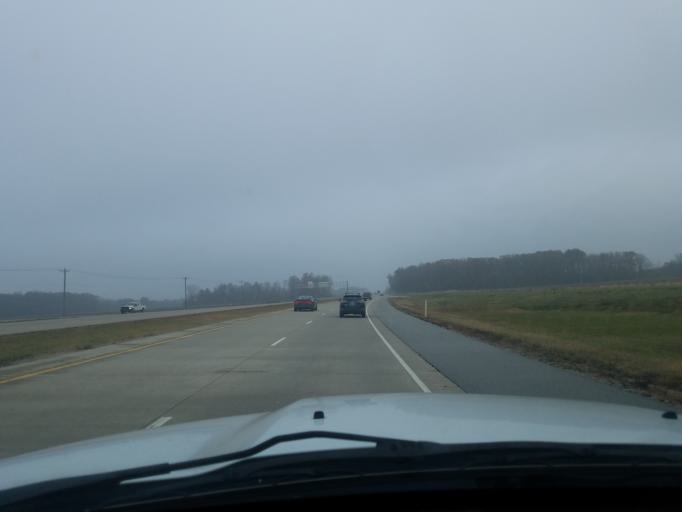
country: US
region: Indiana
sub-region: Howard County
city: Kokomo
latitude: 40.5451
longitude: -86.1270
